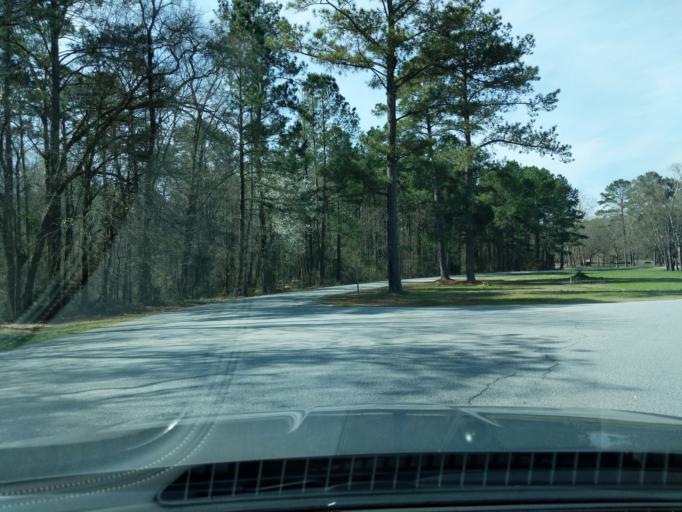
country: US
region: Georgia
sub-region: Columbia County
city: Evans
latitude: 33.6585
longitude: -82.1955
